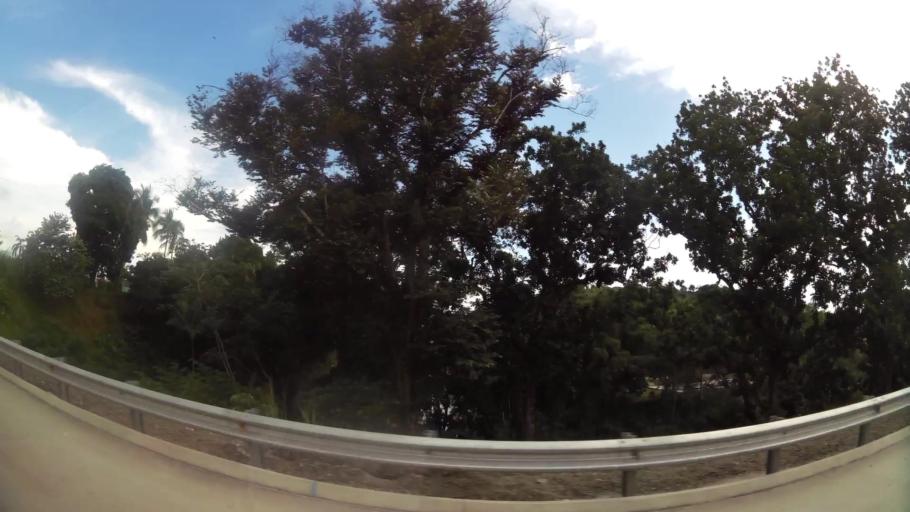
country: PA
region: Panama
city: San Miguelito
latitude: 9.0835
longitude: -79.4467
